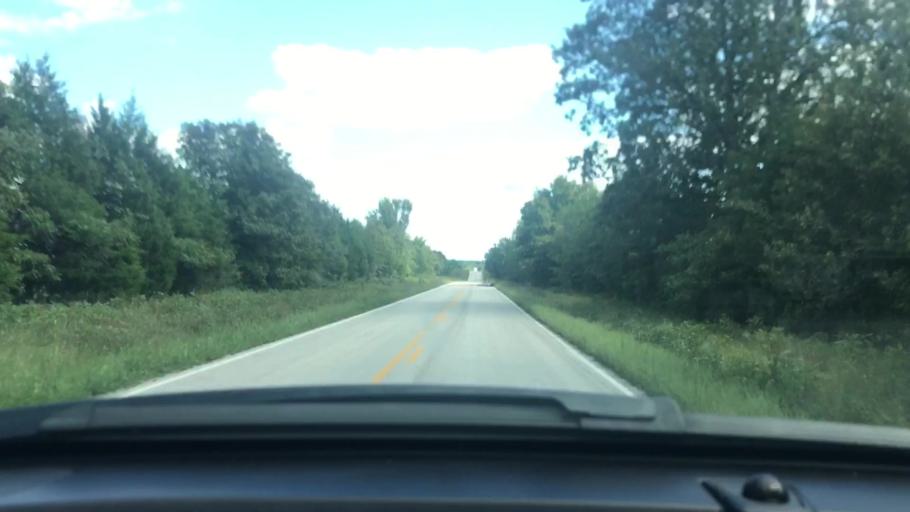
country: US
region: Missouri
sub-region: Wright County
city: Hartville
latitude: 37.3921
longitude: -92.4504
